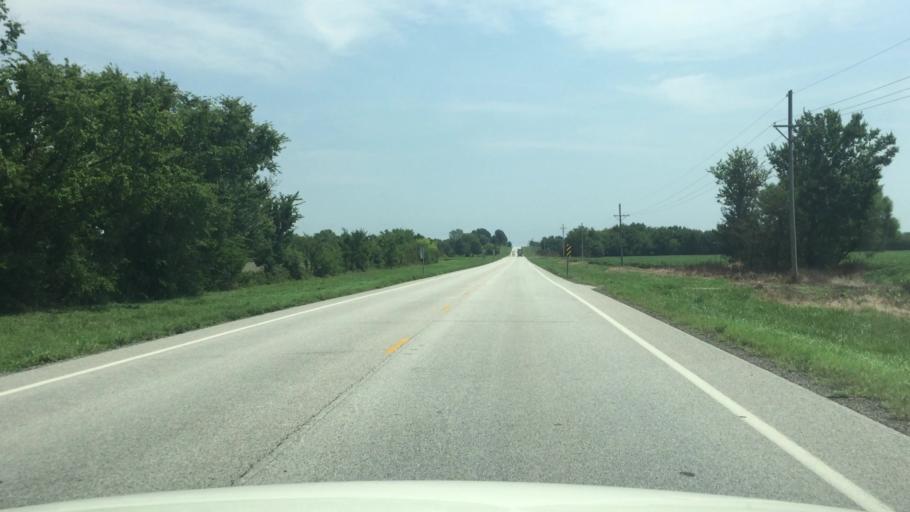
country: US
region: Kansas
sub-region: Cherokee County
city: Columbus
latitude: 37.1780
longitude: -94.8004
